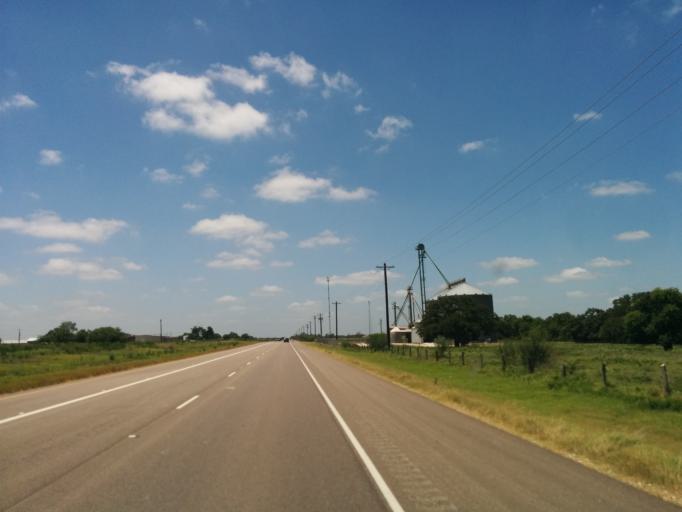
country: US
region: Texas
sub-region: Brazos County
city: Bryan
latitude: 30.8065
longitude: -96.2426
